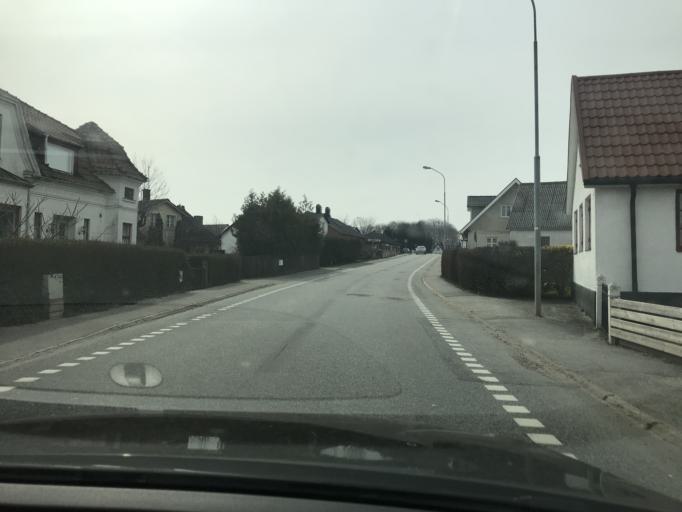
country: SE
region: Skane
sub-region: Skurups Kommun
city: Skivarp
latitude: 55.4237
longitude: 13.5755
